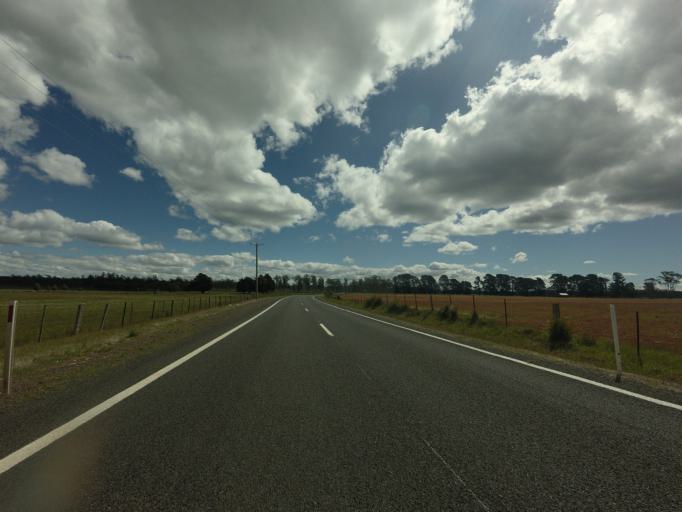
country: AU
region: Tasmania
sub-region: Northern Midlands
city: Evandale
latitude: -41.9895
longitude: 147.6995
